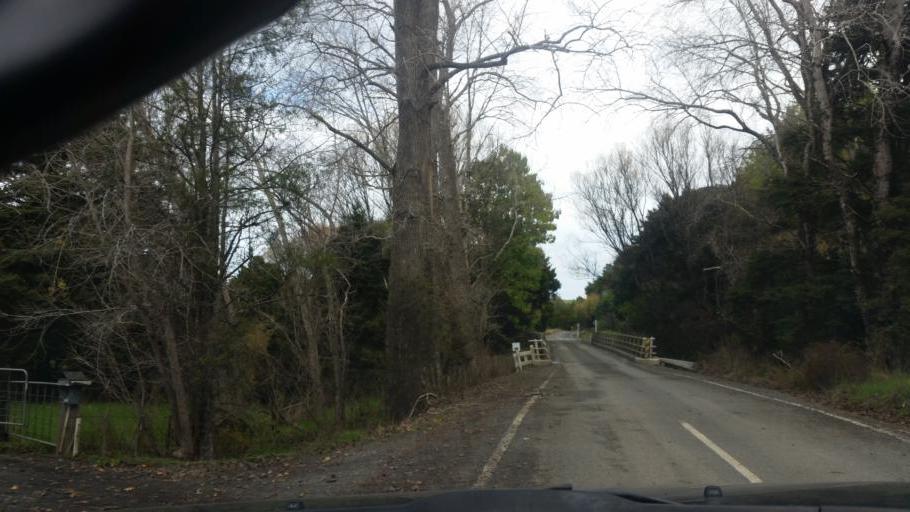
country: NZ
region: Northland
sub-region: Kaipara District
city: Dargaville
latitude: -35.7496
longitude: 173.9049
